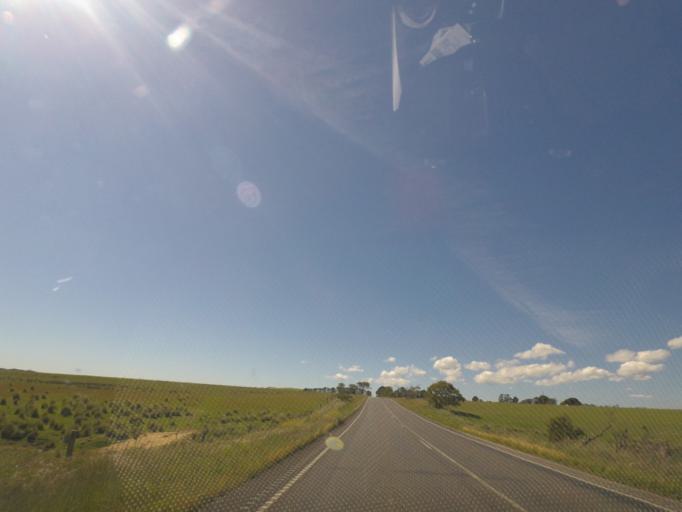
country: AU
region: Victoria
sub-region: Moorabool
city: Bacchus Marsh
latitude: -37.7767
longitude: 144.2163
